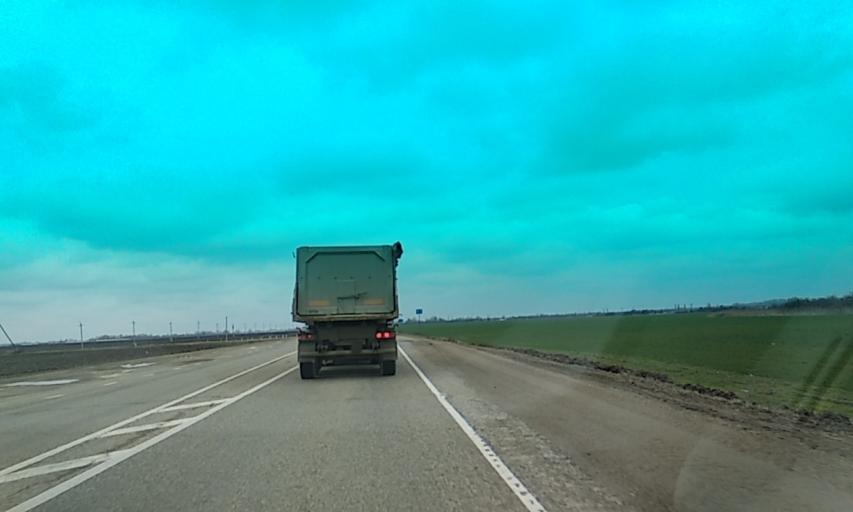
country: RU
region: Adygeya
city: Beloye
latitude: 45.0297
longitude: 39.6821
